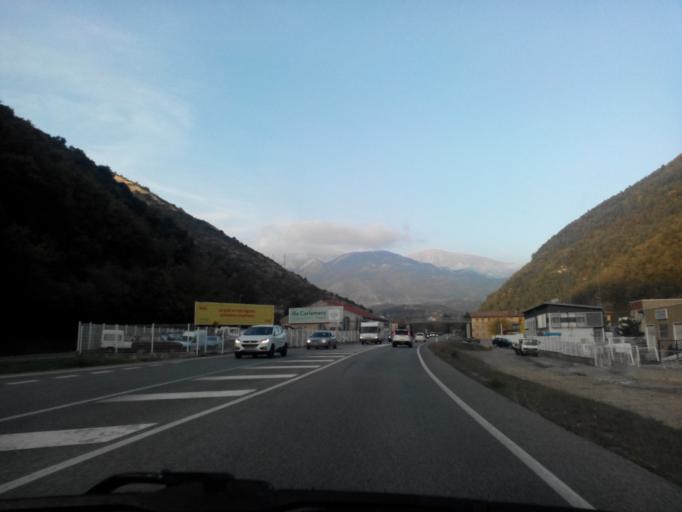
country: ES
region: Catalonia
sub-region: Provincia de Barcelona
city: Guardiola de Bergueda
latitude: 42.2183
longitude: 1.8696
